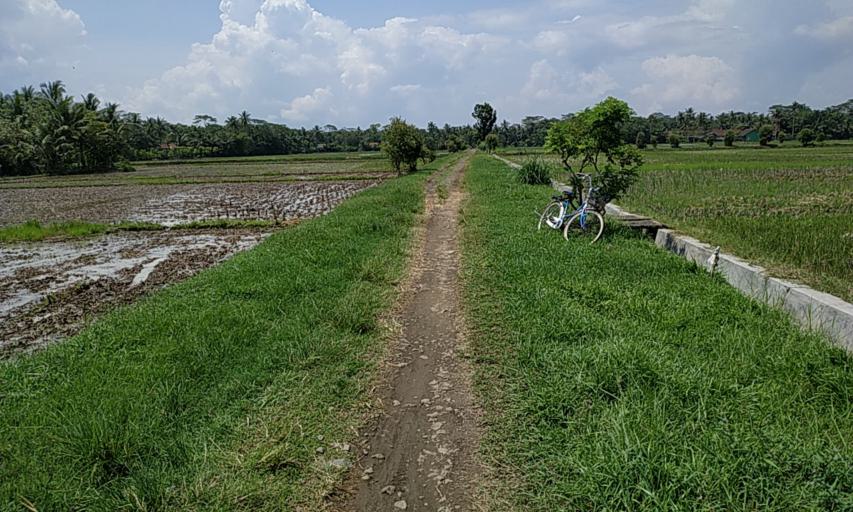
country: ID
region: Central Java
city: Cipari
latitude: -7.5310
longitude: 108.7950
